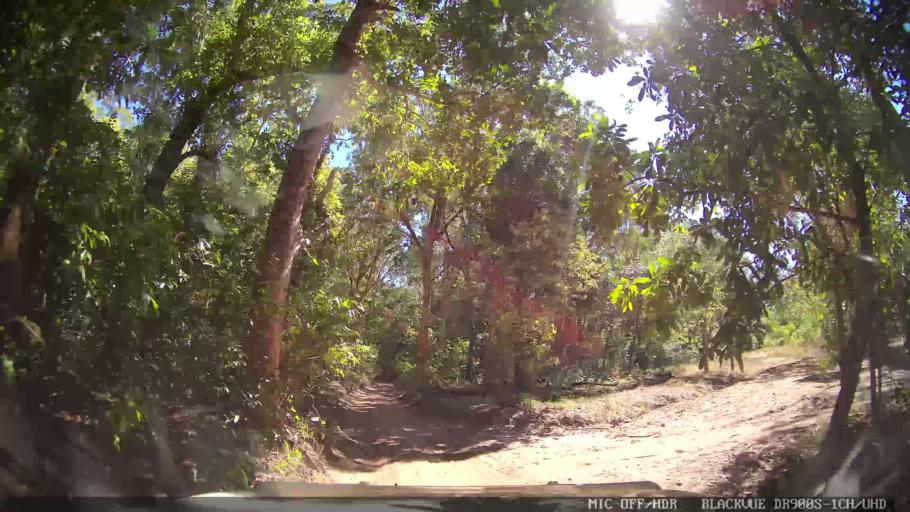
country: AU
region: Queensland
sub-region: Torres
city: Thursday Island
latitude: -10.8278
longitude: 142.3998
